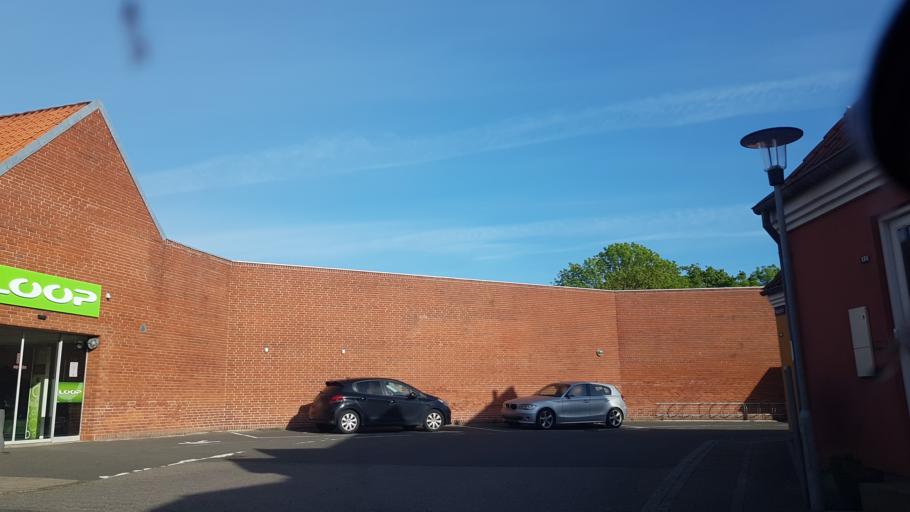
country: DK
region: Zealand
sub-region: Slagelse Kommune
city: Korsor
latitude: 55.3283
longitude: 11.1384
